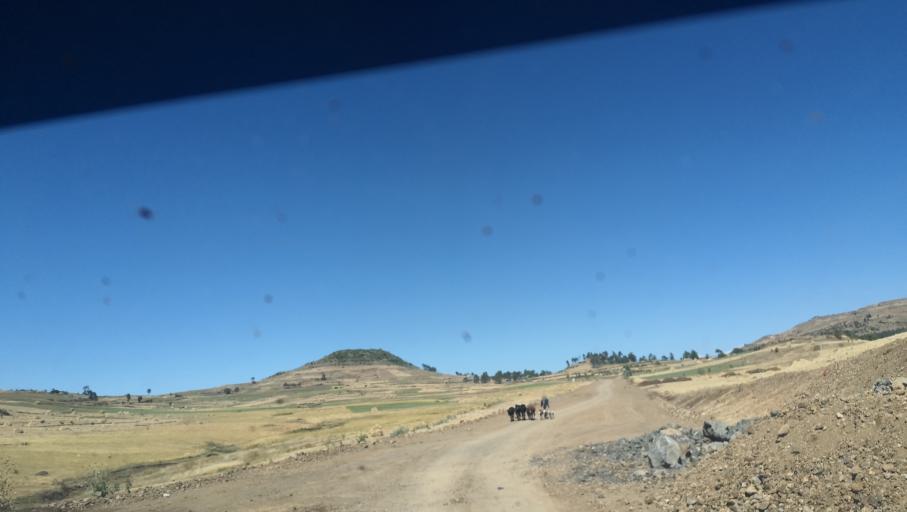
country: ET
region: Amhara
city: Debre Tabor
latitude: 11.5609
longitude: 38.1401
